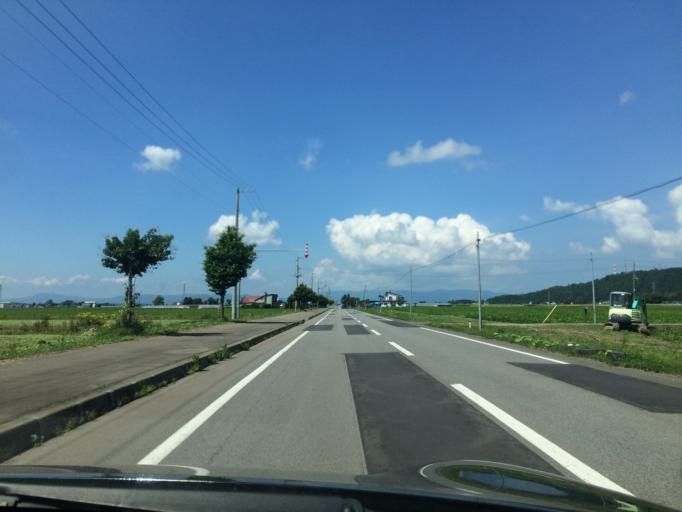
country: JP
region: Hokkaido
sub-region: Asahikawa-shi
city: Asahikawa
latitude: 43.7479
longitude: 142.4619
